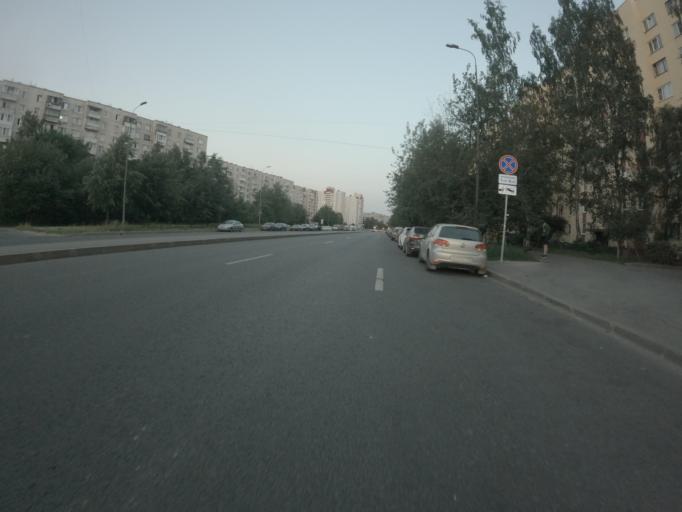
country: RU
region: St.-Petersburg
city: Krasnogvargeisky
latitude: 59.9239
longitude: 30.4752
